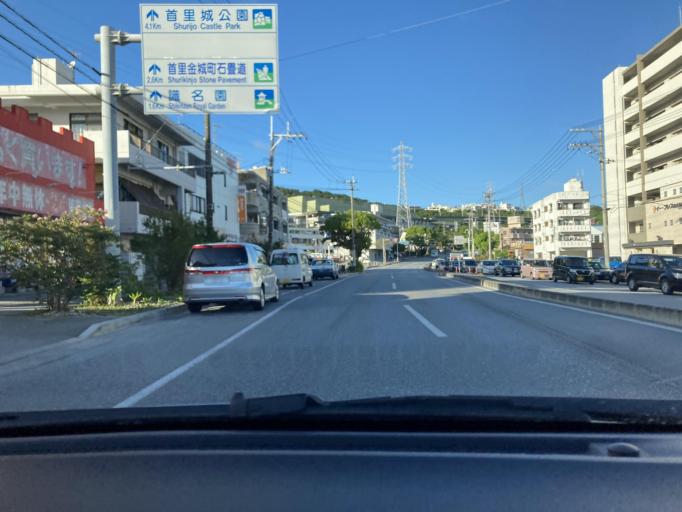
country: JP
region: Okinawa
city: Tomigusuku
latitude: 26.1992
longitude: 127.7139
